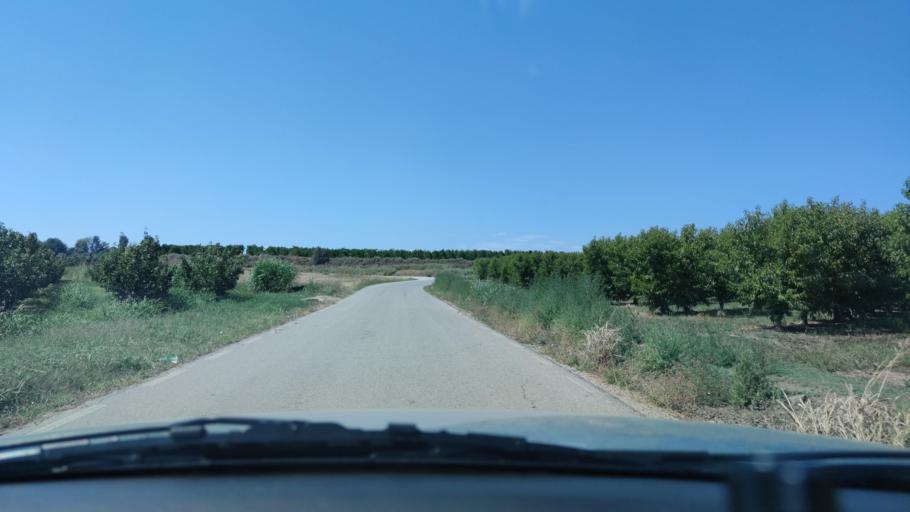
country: ES
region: Catalonia
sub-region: Provincia de Lleida
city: Torrefarrera
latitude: 41.6804
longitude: 0.6168
